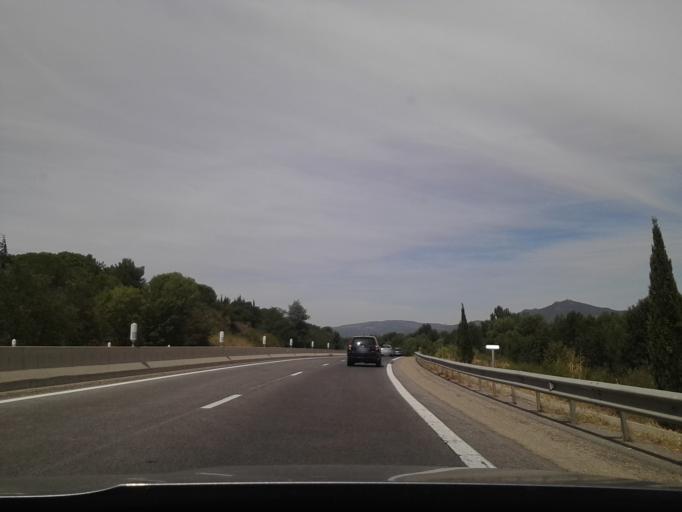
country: FR
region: Languedoc-Roussillon
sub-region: Departement des Pyrenees-Orientales
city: Pezilla-la-Riviere
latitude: 42.6816
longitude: 2.7760
